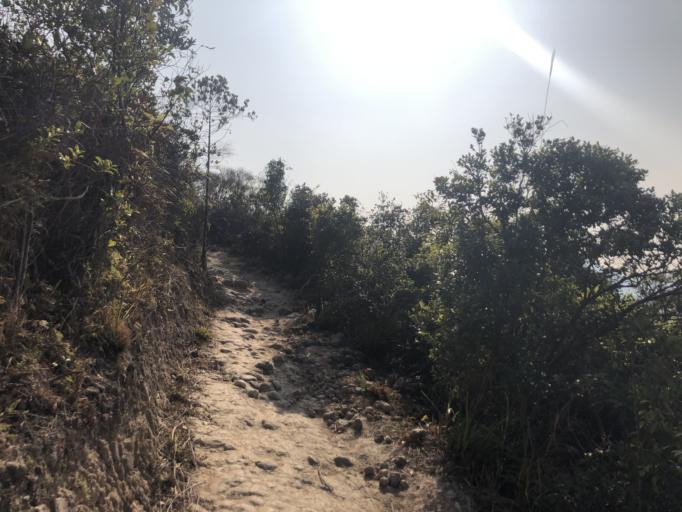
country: HK
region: Sai Kung
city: Sai Kung
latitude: 22.3623
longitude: 114.2935
